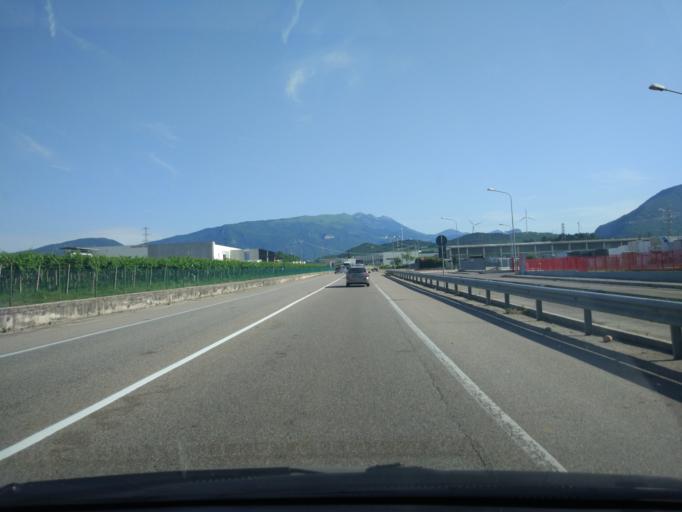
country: IT
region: Veneto
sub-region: Provincia di Verona
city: Volargne
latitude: 45.5338
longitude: 10.8018
